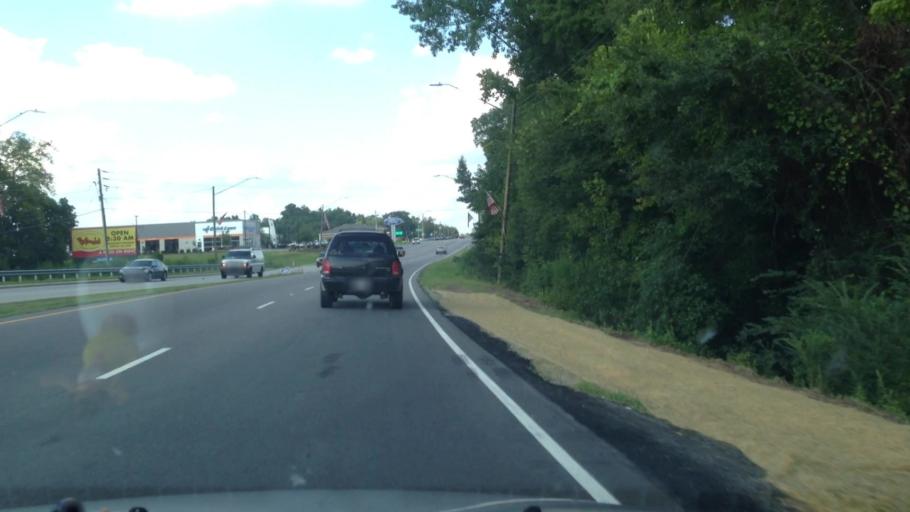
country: US
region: North Carolina
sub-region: Harnett County
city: Lillington
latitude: 35.4105
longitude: -78.8109
